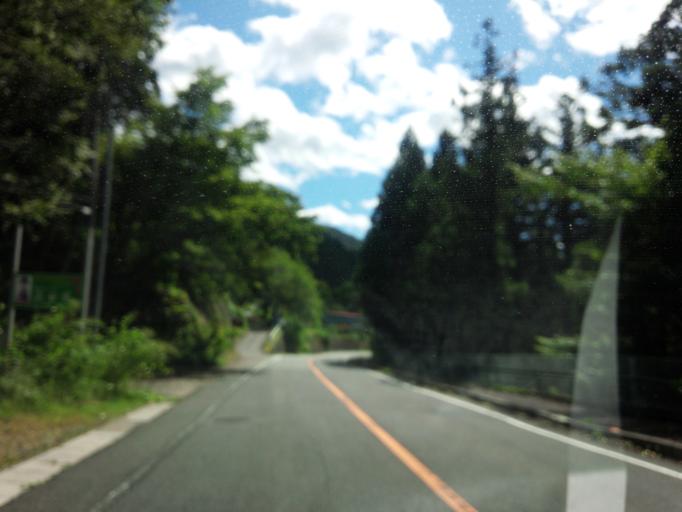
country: JP
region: Gunma
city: Nakanojomachi
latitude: 36.6713
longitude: 138.7873
